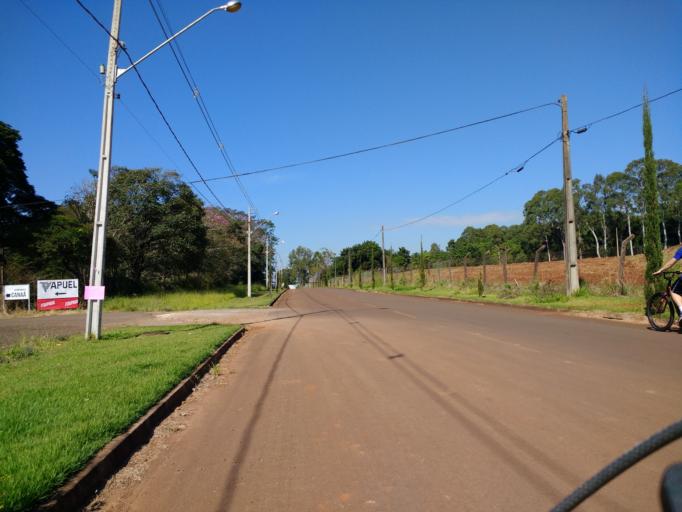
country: BR
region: Parana
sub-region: Londrina
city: Londrina
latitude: -23.3631
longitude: -51.1954
